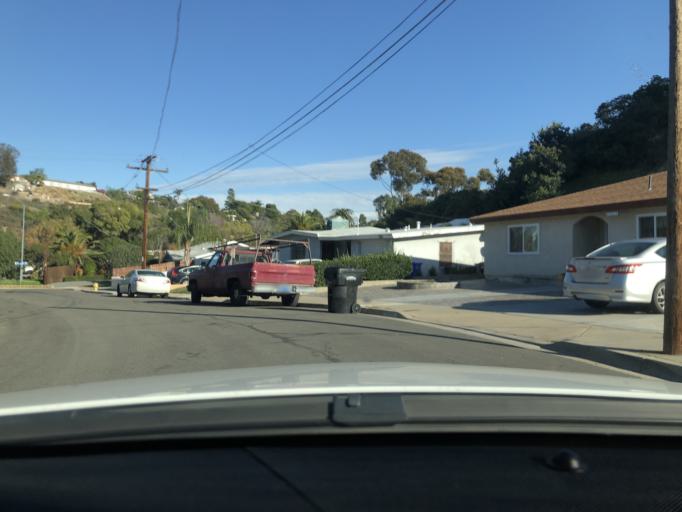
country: US
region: California
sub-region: San Diego County
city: Lemon Grove
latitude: 32.7507
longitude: -117.0639
